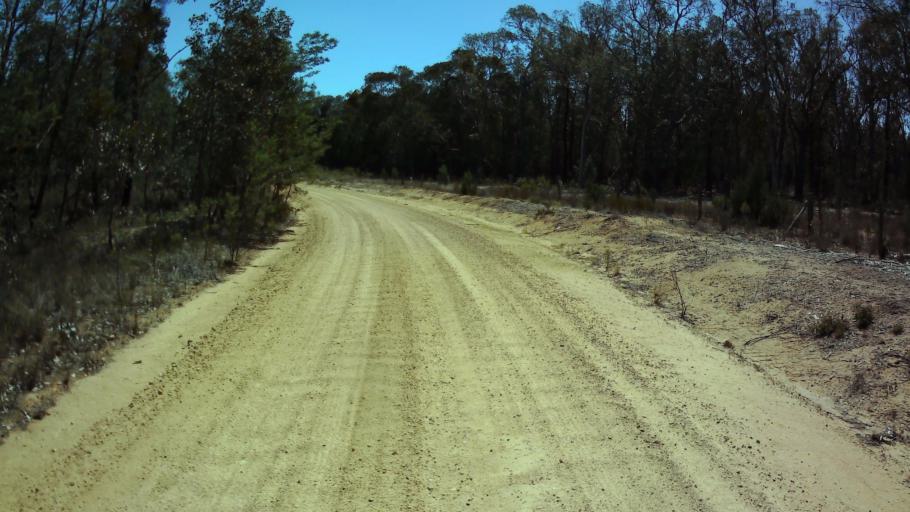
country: AU
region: New South Wales
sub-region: Cowra
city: Cowra
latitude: -33.8478
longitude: 148.4505
